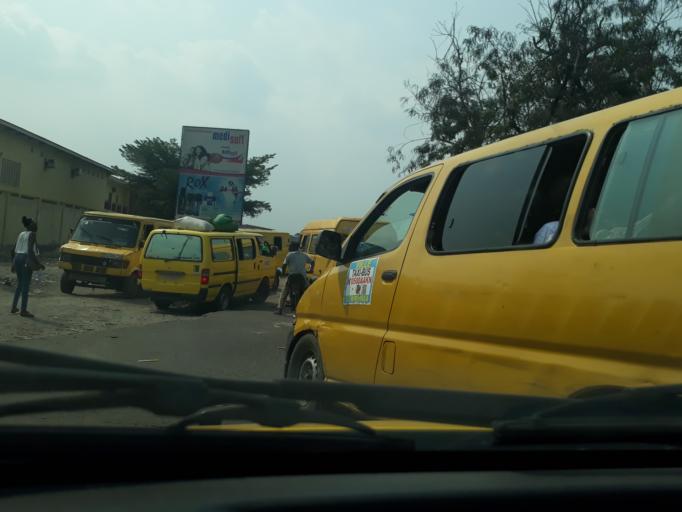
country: CD
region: Kinshasa
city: Kinshasa
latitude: -4.3312
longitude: 15.3208
